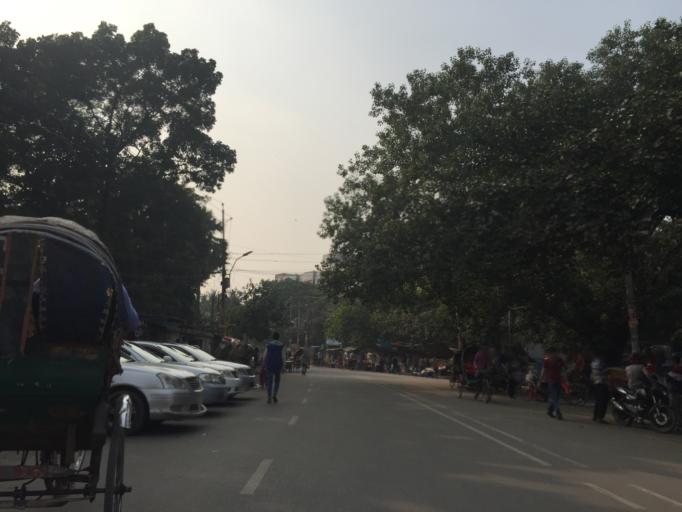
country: BD
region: Dhaka
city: Azimpur
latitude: 23.7323
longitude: 90.3826
